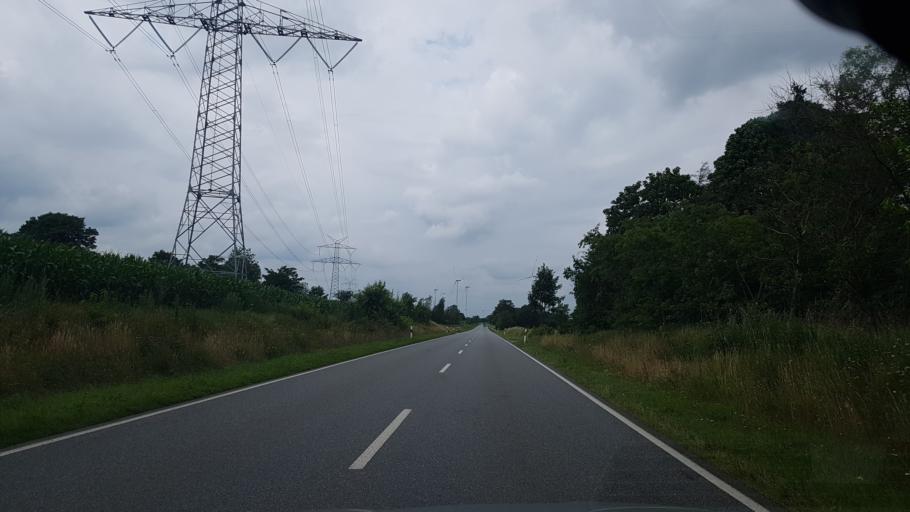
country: DE
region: Schleswig-Holstein
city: Jardelund
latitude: 54.8321
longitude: 9.2156
